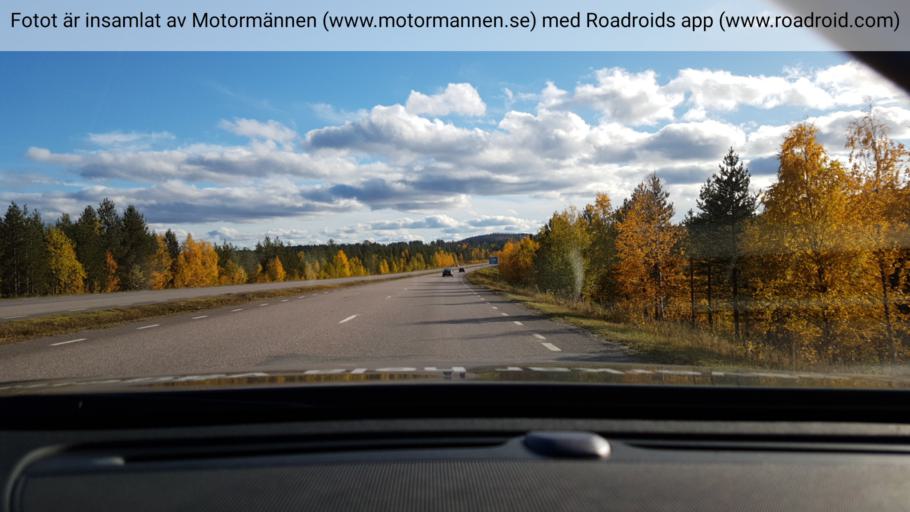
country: SE
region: Norrbotten
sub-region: Gallivare Kommun
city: Malmberget
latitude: 67.1551
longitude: 20.6621
